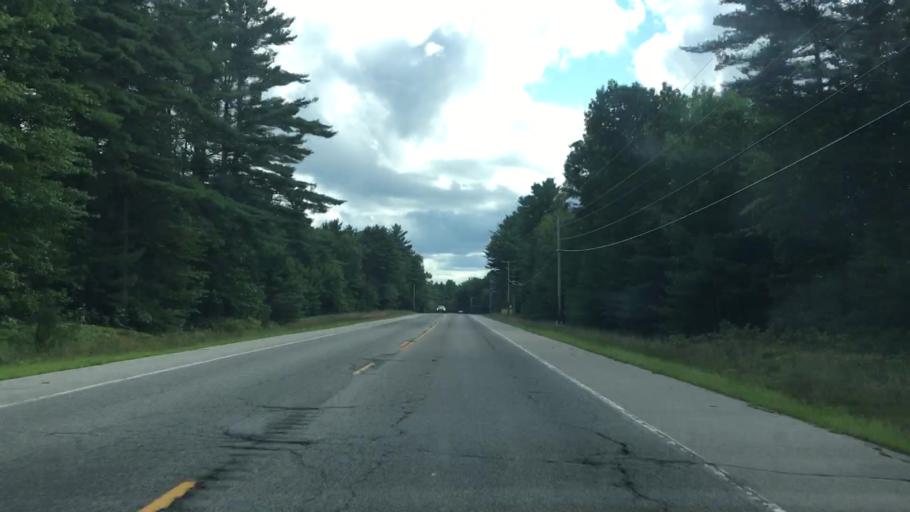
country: US
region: Maine
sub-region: York County
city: South Sanford
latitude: 43.3823
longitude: -70.7404
